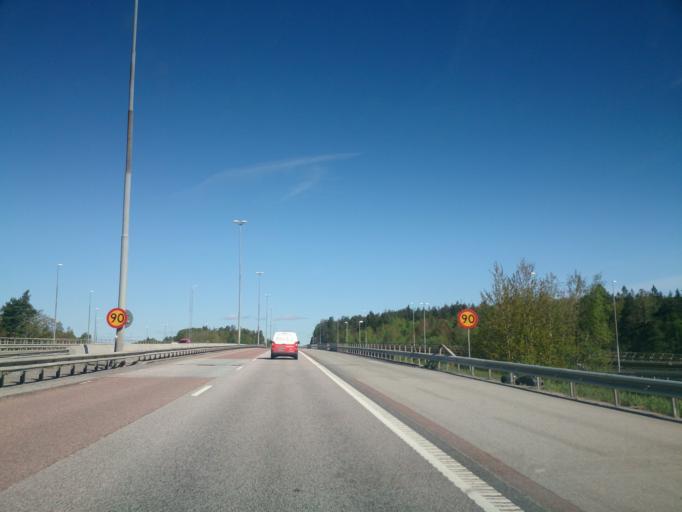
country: SE
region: Stockholm
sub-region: Haninge Kommun
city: Handen
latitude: 59.2280
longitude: 18.1259
